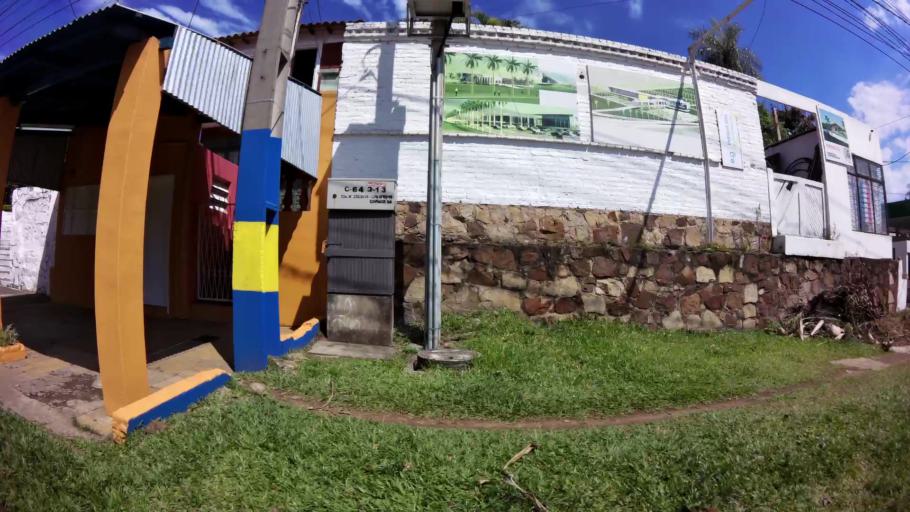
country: PY
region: Central
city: San Lorenzo
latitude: -25.2747
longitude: -57.4965
